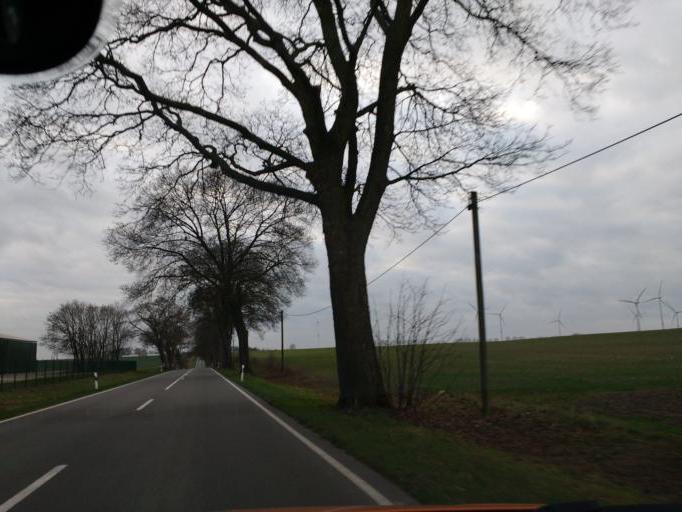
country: DE
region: Brandenburg
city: Wriezen
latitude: 52.6842
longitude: 14.0946
